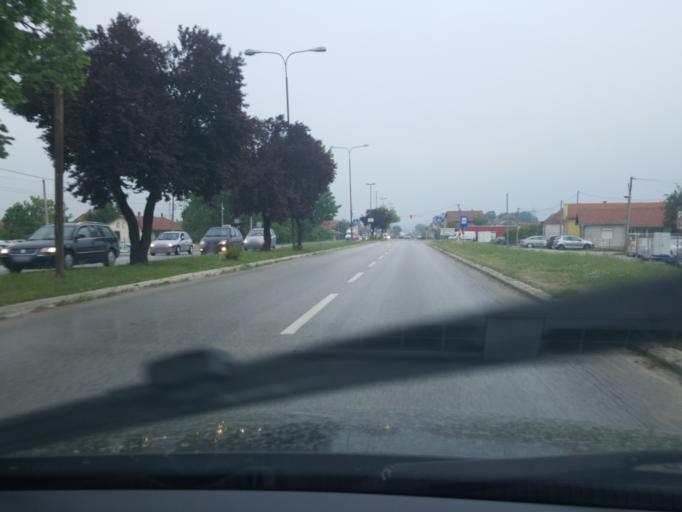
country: RS
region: Central Serbia
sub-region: Kolubarski Okrug
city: Valjevo
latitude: 44.2800
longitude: 19.9241
